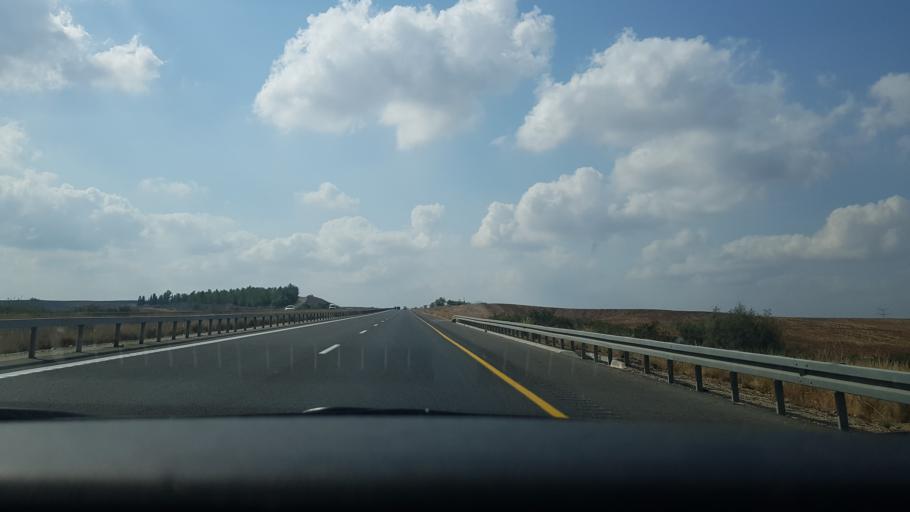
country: IL
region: Southern District
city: Qiryat Gat
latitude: 31.6867
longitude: 34.8100
